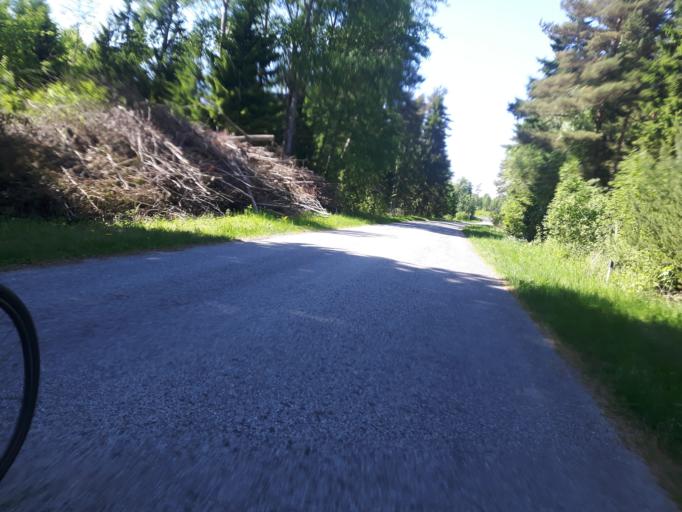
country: EE
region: Laeaene-Virumaa
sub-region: Haljala vald
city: Haljala
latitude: 59.5504
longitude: 26.3729
